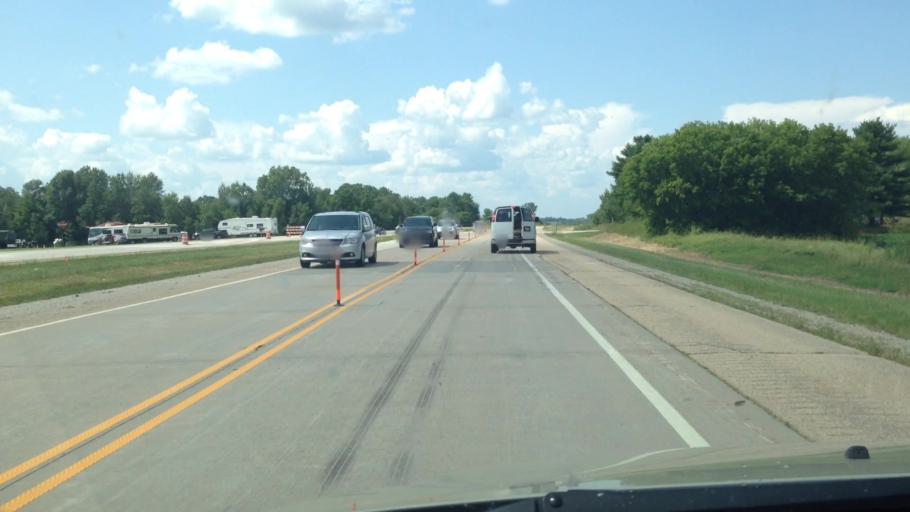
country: US
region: Wisconsin
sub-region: Shawano County
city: Bonduel
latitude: 44.7047
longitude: -88.3729
